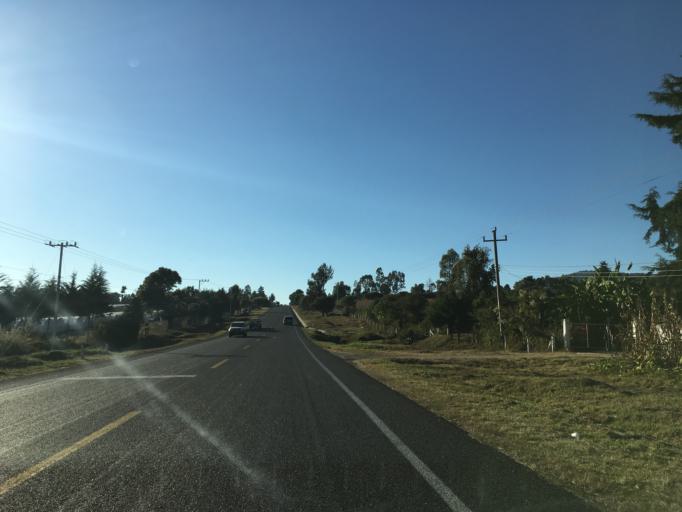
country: MX
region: Michoacan
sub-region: Zitacuaro
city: Puentecillas (Tercera Manzana de Zirahuato)
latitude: 19.4857
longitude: -100.4029
